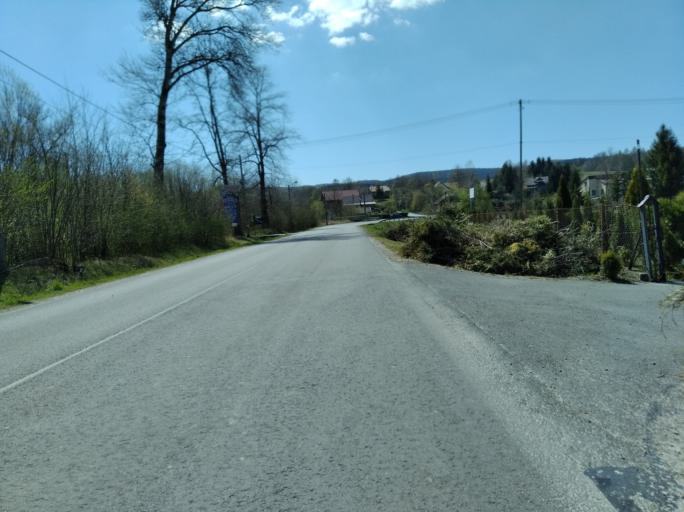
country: PL
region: Subcarpathian Voivodeship
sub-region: Powiat brzozowski
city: Dydnia
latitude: 49.6833
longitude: 22.1861
